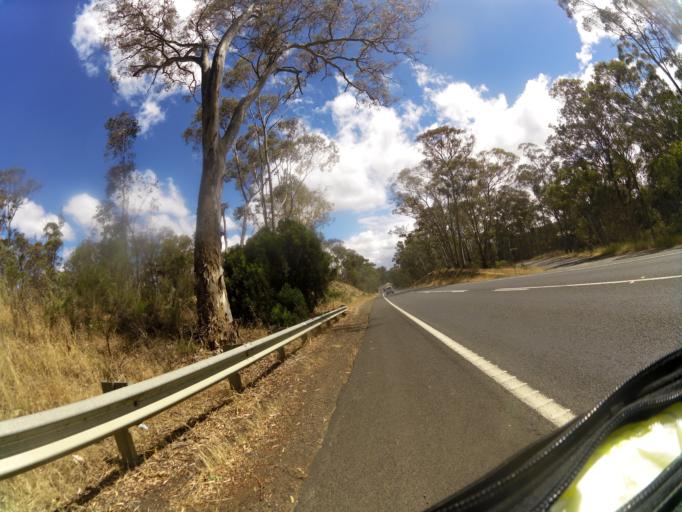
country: AU
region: Victoria
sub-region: Mount Alexander
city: Castlemaine
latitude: -37.0345
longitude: 144.2307
